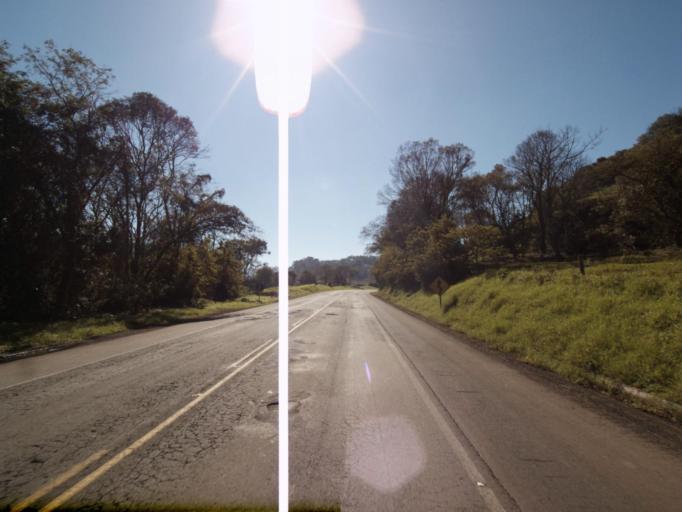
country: BR
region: Rio Grande do Sul
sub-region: Frederico Westphalen
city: Frederico Westphalen
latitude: -27.0259
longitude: -53.2324
